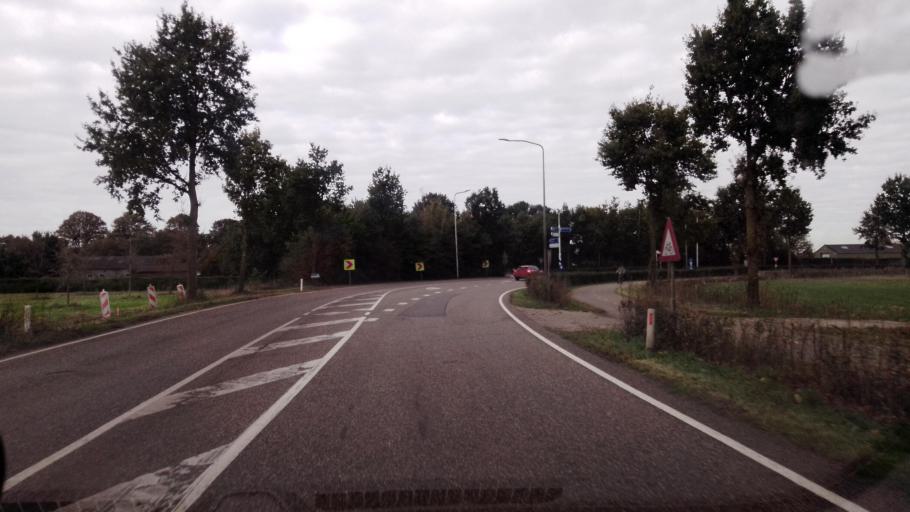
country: NL
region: Limburg
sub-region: Gemeente Venlo
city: Venlo
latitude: 51.4192
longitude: 6.1090
